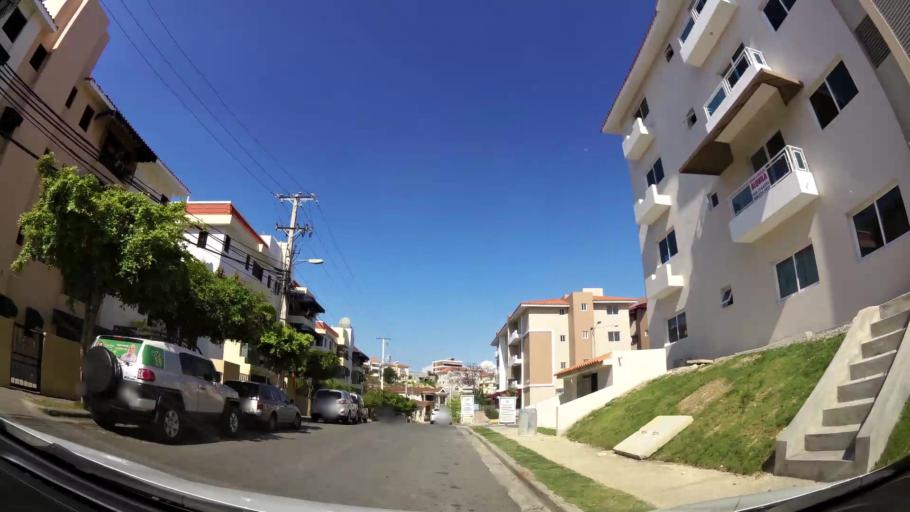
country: DO
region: Nacional
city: Bella Vista
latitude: 18.4592
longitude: -69.9831
